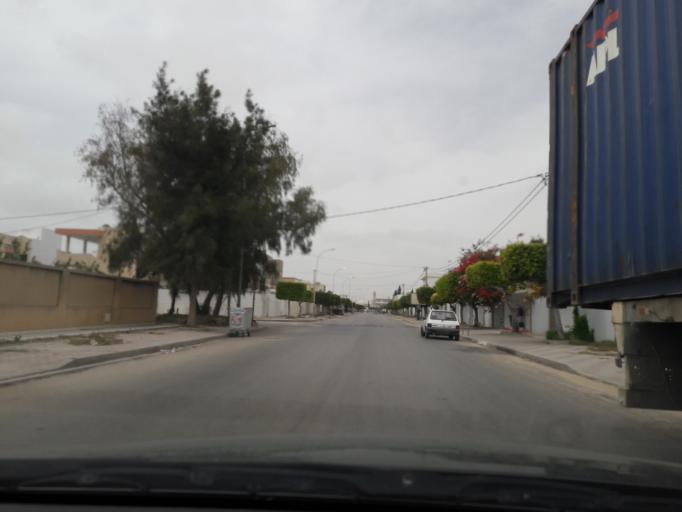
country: TN
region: Safaqis
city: Al Qarmadah
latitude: 34.7971
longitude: 10.7526
